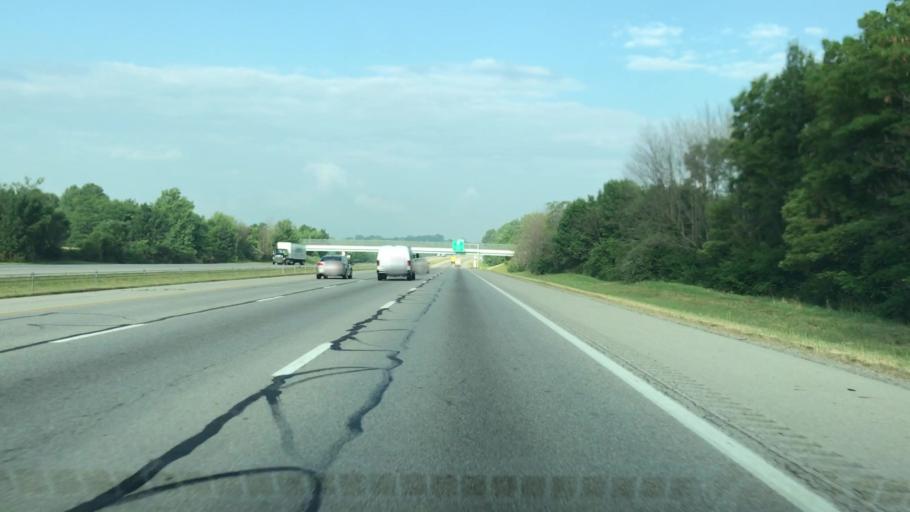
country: US
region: Ohio
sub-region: Clark County
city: Lisbon
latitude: 39.9348
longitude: -83.5861
